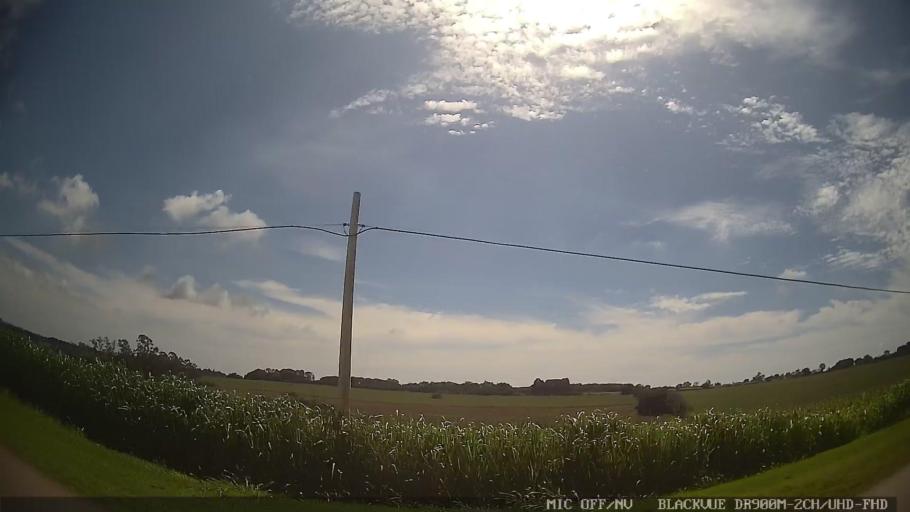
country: BR
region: Sao Paulo
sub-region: Tiete
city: Tiete
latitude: -23.1256
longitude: -47.6980
